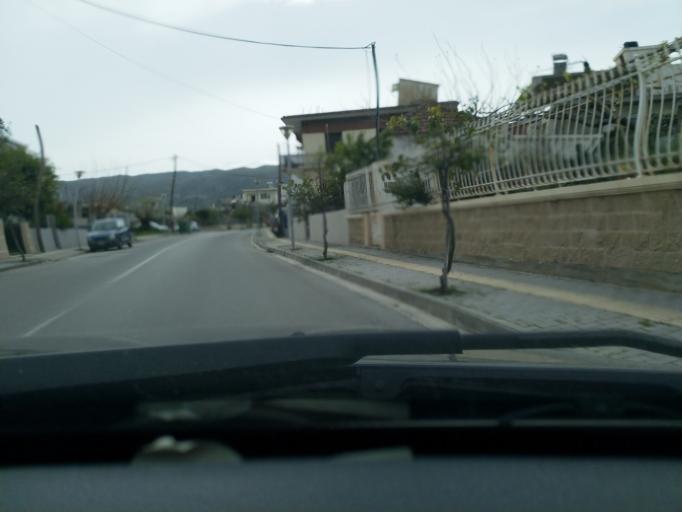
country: GR
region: Crete
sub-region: Nomos Chanias
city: Mournies
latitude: 35.4951
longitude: 24.0226
